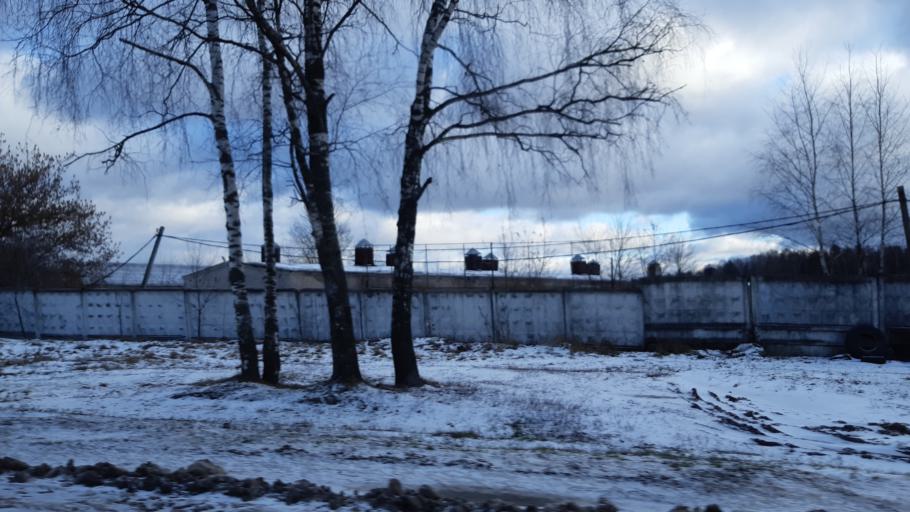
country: RU
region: Moskovskaya
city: Noginsk-9
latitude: 55.9468
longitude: 38.5521
